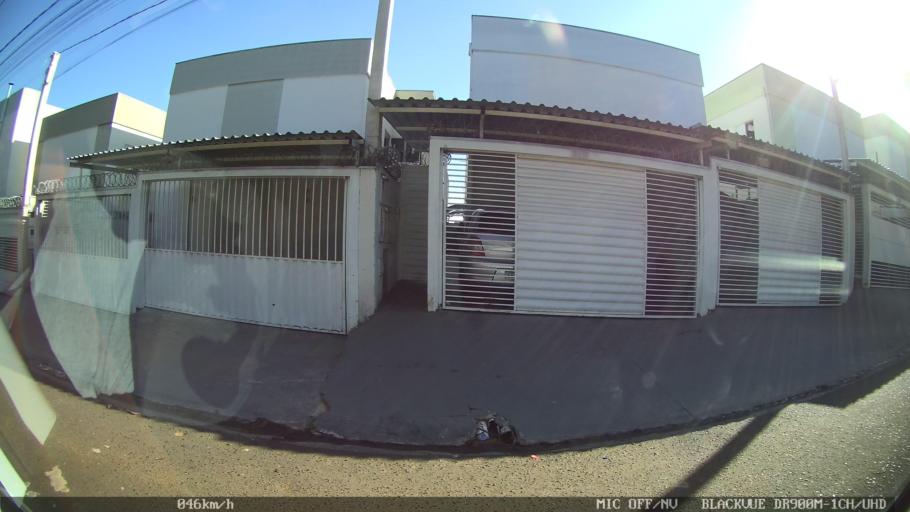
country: BR
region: Sao Paulo
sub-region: Franca
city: Franca
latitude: -20.4843
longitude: -47.4213
